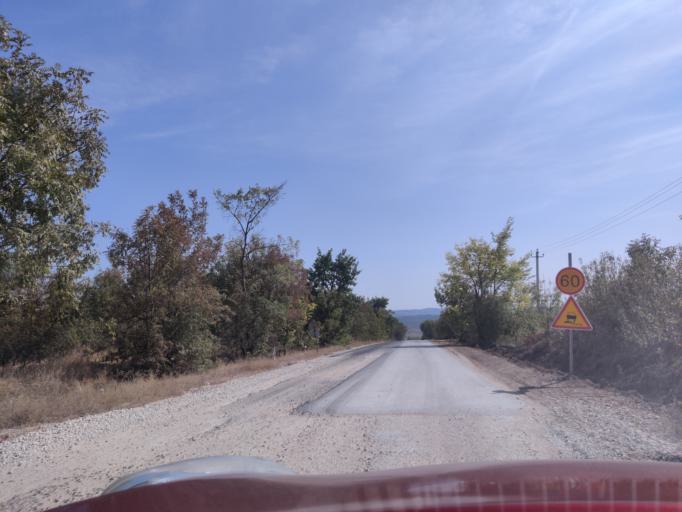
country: MD
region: Ungheni
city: Ungheni
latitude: 47.2639
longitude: 27.9799
